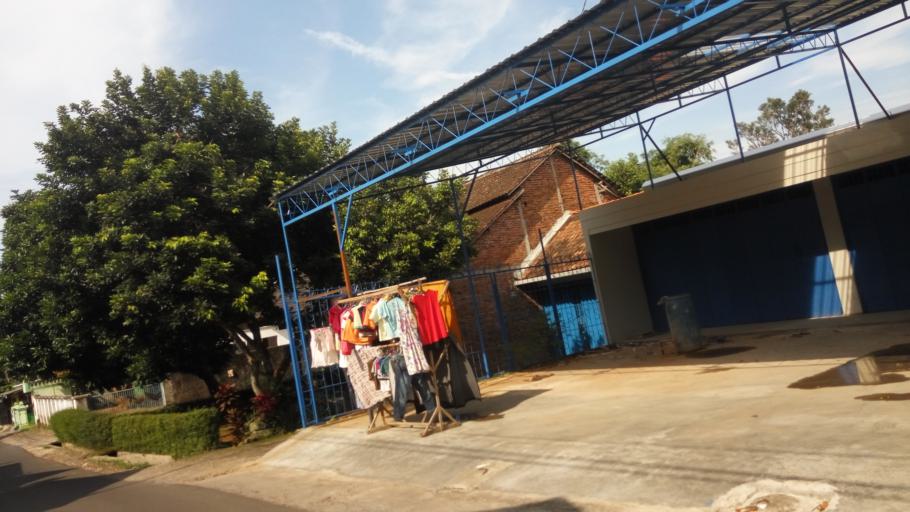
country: ID
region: Central Java
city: Ungaran
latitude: -7.1457
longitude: 110.4116
